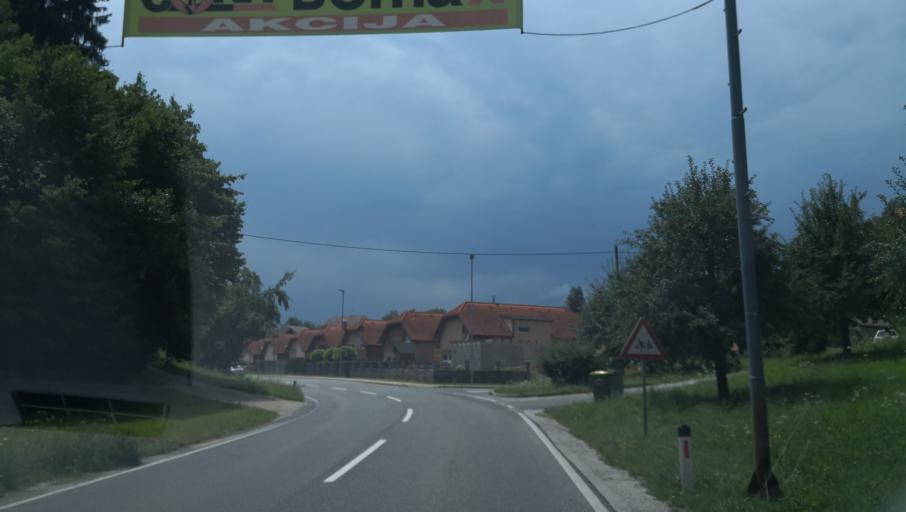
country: SI
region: Ivancna Gorica
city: Ivancna Gorica
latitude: 45.9061
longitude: 14.8001
